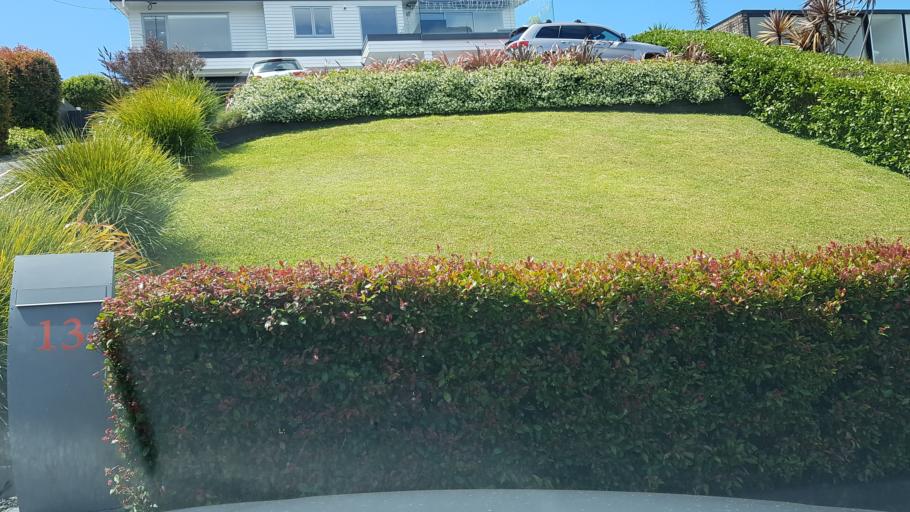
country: NZ
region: Auckland
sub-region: Auckland
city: North Shore
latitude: -36.8123
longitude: 174.7412
